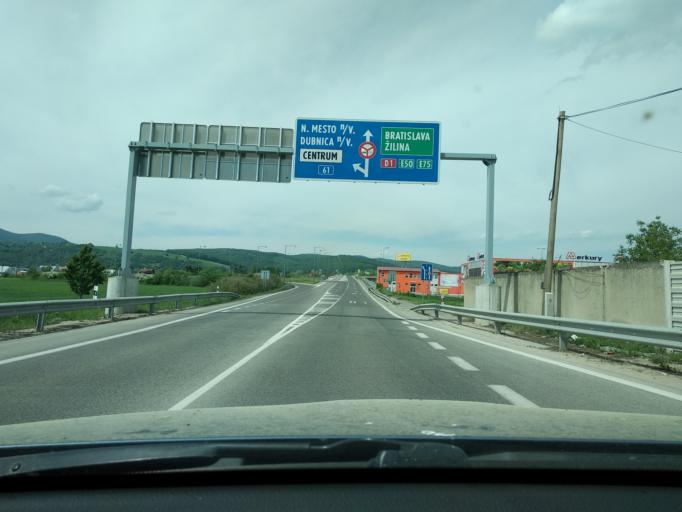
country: SK
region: Trenciansky
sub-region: Okres Trencin
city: Trencin
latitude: 48.8904
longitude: 18.0066
